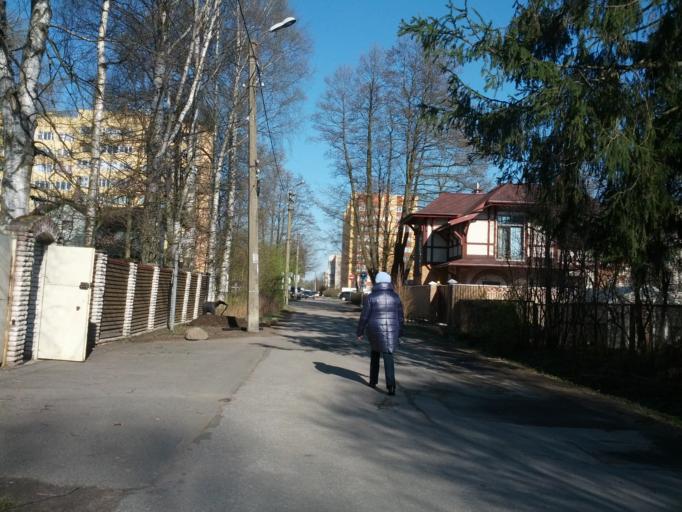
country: RU
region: St.-Petersburg
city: Sestroretsk
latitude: 60.0891
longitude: 29.9451
